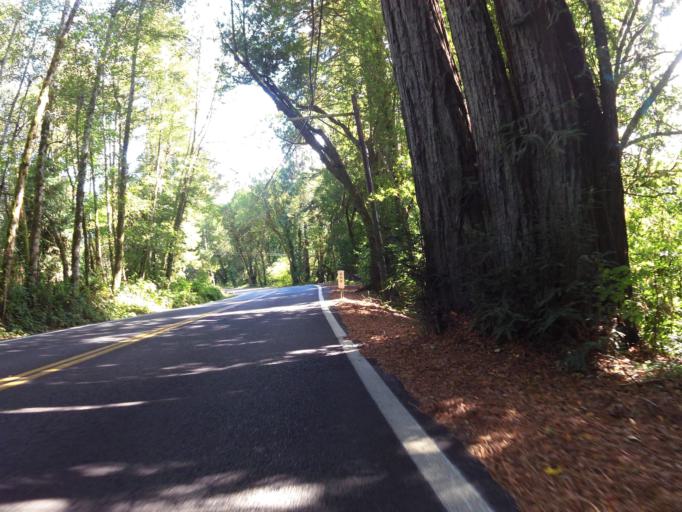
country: US
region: California
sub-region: Del Norte County
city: Bertsch-Oceanview
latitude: 41.8505
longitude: -124.1203
